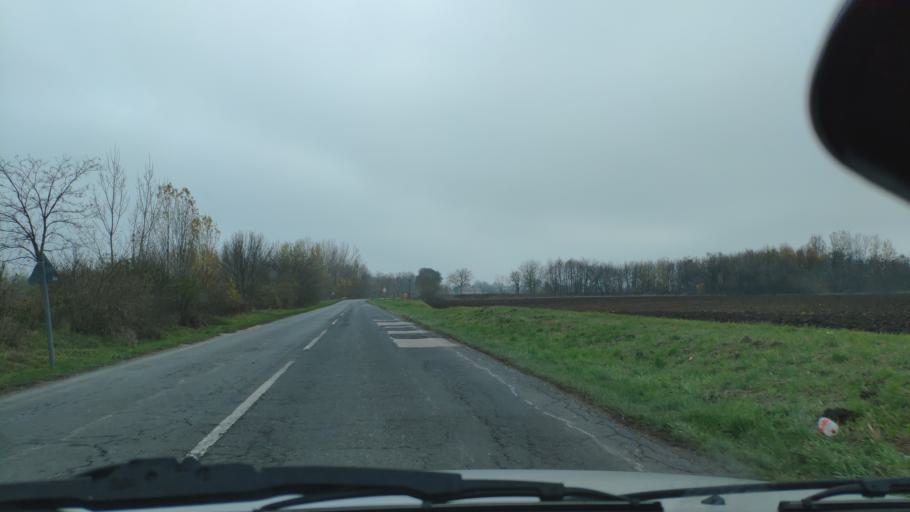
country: HU
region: Somogy
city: Balatonbereny
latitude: 46.6826
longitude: 17.2834
